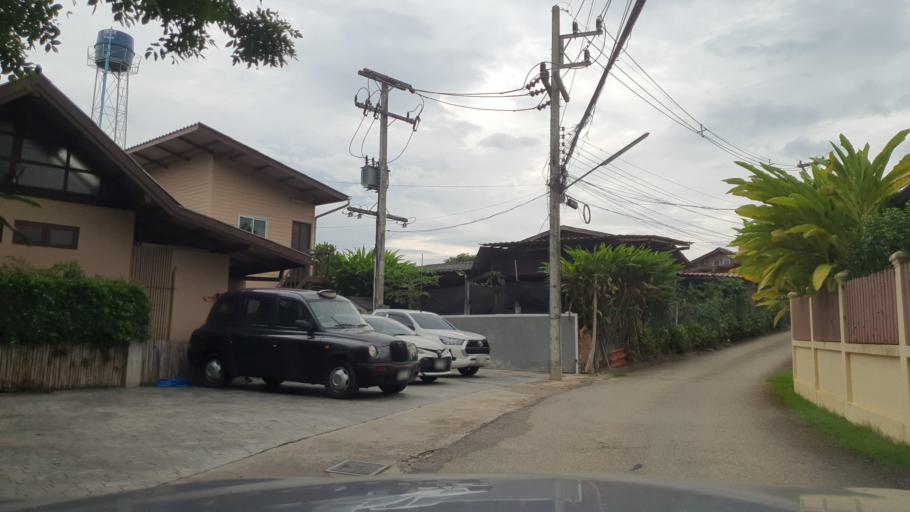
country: TH
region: Chiang Mai
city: Chiang Mai
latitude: 18.9275
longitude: 98.9076
